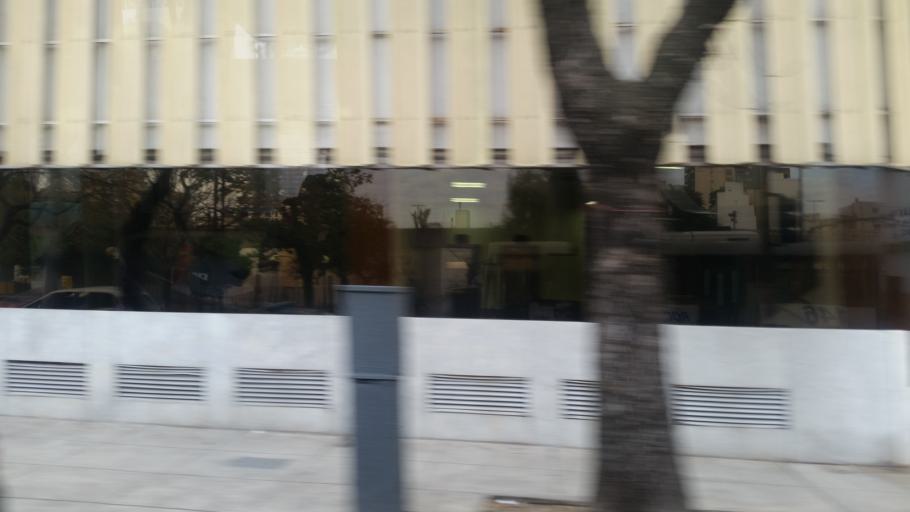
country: AR
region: Buenos Aires F.D.
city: Buenos Aires
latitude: -34.6079
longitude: -58.4106
